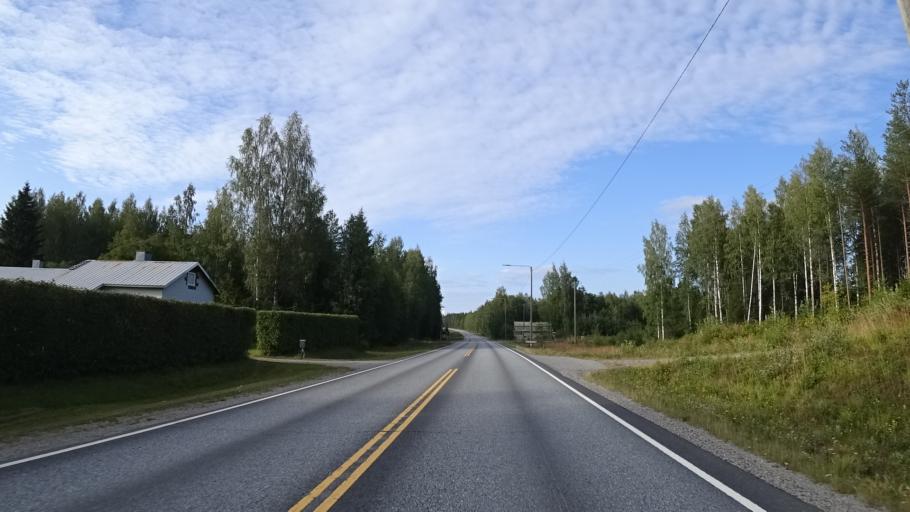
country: FI
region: North Karelia
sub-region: Joensuu
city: Eno
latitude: 62.8639
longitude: 30.1994
